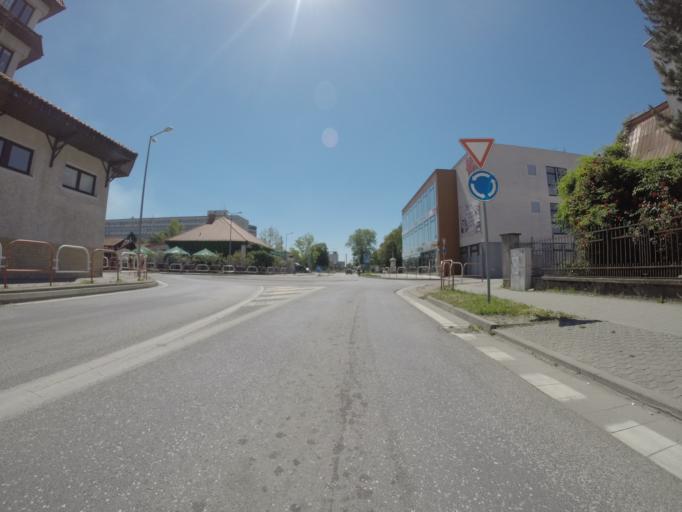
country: SK
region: Trnavsky
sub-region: Okres Galanta
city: Galanta
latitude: 48.1905
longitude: 17.7243
